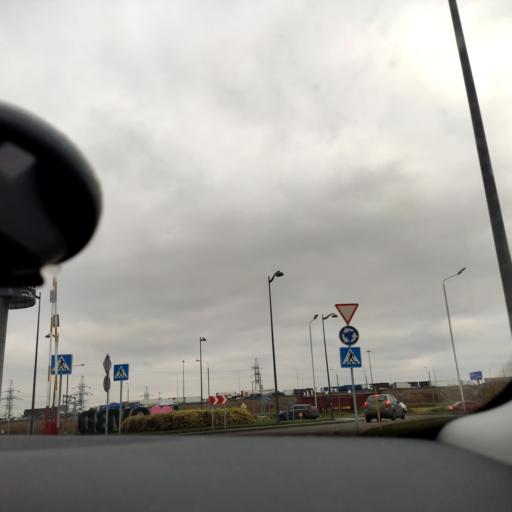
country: RU
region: Moskovskaya
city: Lyubertsy
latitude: 55.6604
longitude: 37.8839
